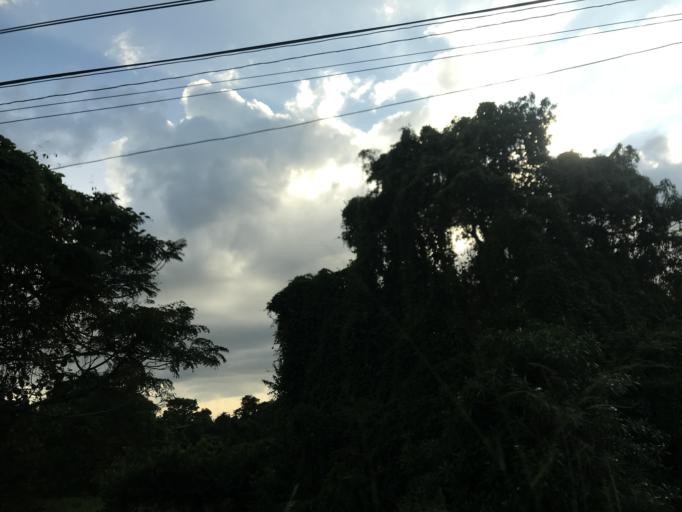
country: LK
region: Western
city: Gampaha
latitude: 7.1012
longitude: 79.9803
